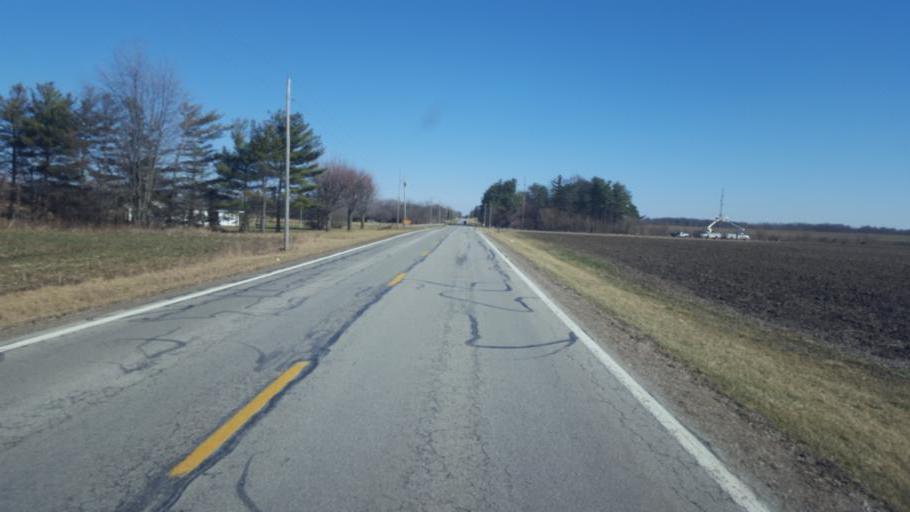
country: US
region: Ohio
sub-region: Wyandot County
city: Upper Sandusky
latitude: 40.6436
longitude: -83.3268
